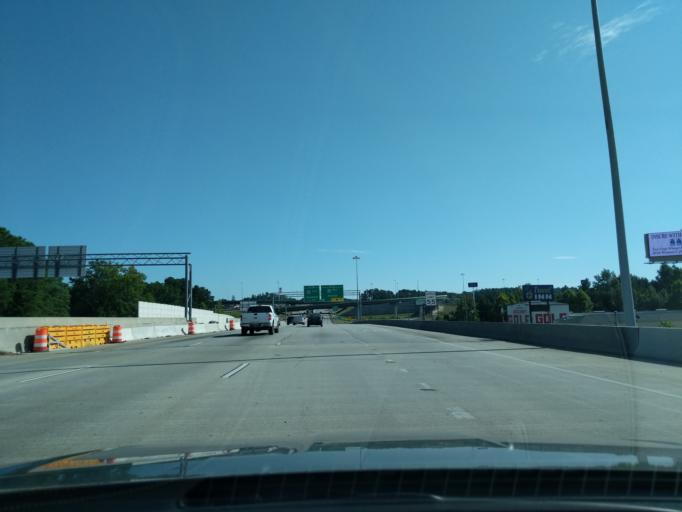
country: US
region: Georgia
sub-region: Columbia County
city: Martinez
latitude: 33.4984
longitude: -82.0865
